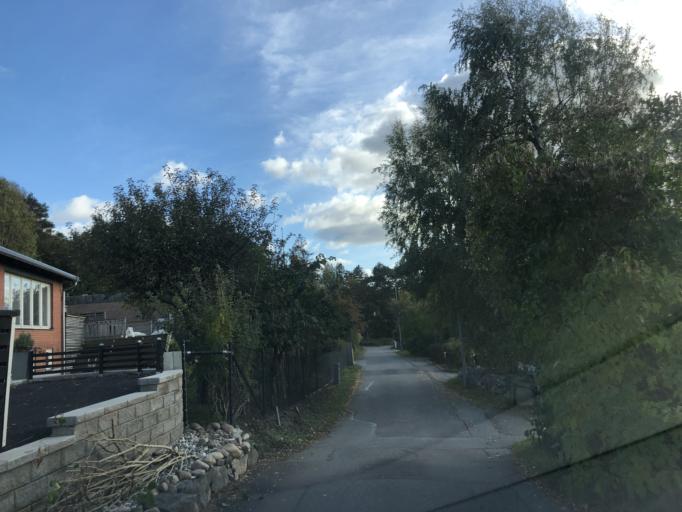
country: SE
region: Vaestra Goetaland
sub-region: Goteborg
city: Majorna
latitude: 57.6320
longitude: 11.9409
